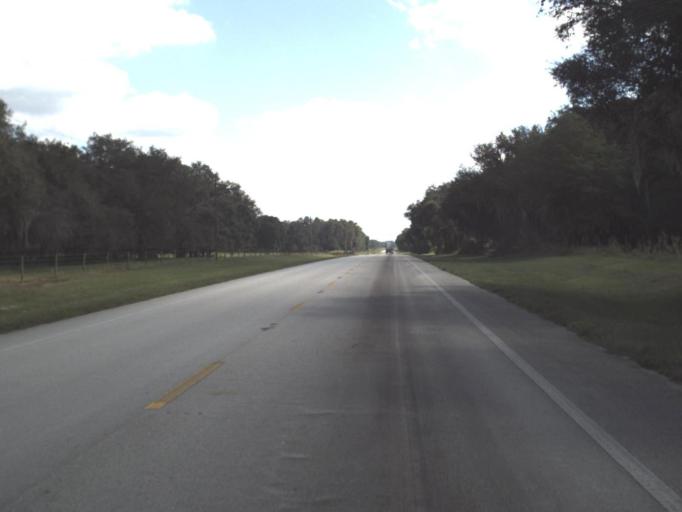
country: US
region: Florida
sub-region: Hardee County
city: Zolfo Springs
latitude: 27.4517
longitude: -81.6361
